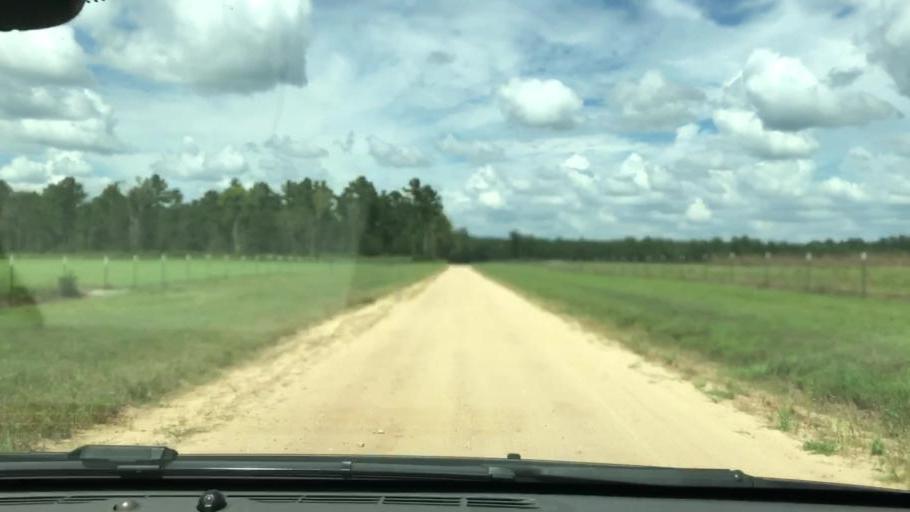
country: US
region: Georgia
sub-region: Quitman County
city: Georgetown
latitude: 32.0316
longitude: -85.0367
